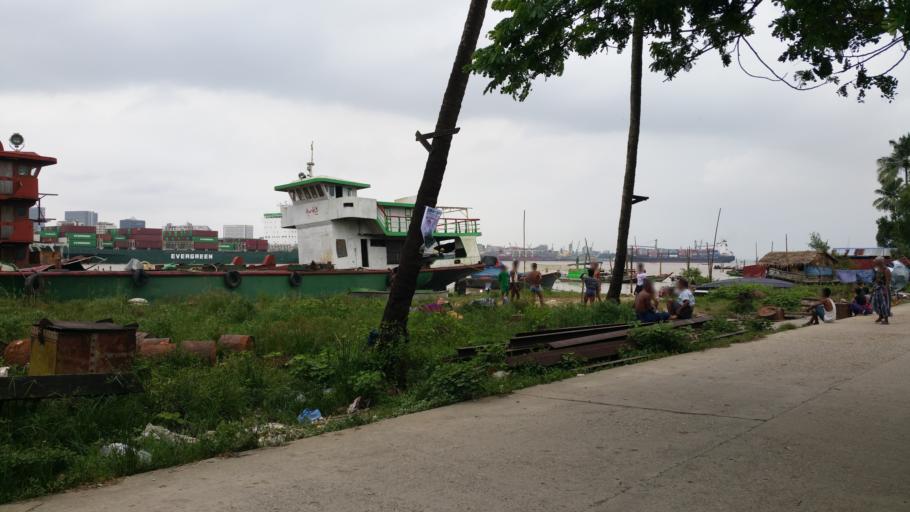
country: MM
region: Yangon
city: Yangon
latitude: 16.7666
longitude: 96.1415
